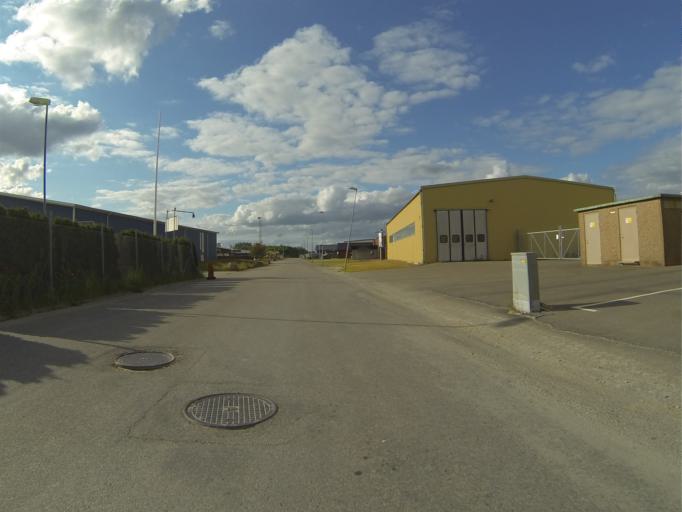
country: SE
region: Skane
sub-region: Staffanstorps Kommun
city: Staffanstorp
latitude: 55.6532
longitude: 13.2328
